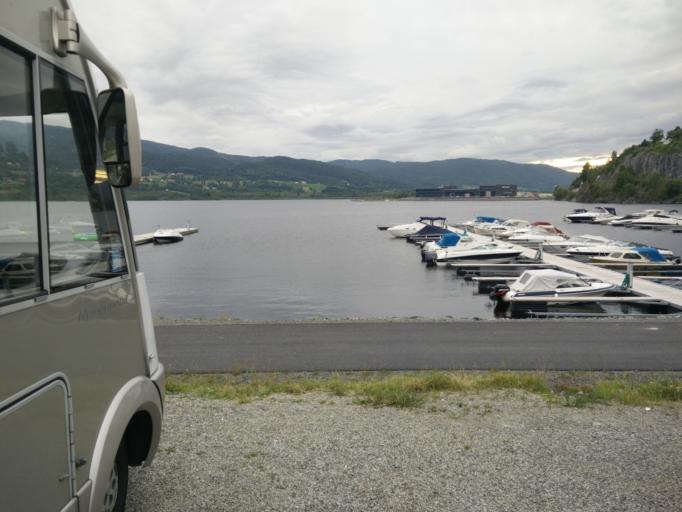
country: NO
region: Telemark
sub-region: Notodden
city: Notodden
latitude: 59.5594
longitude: 9.2480
